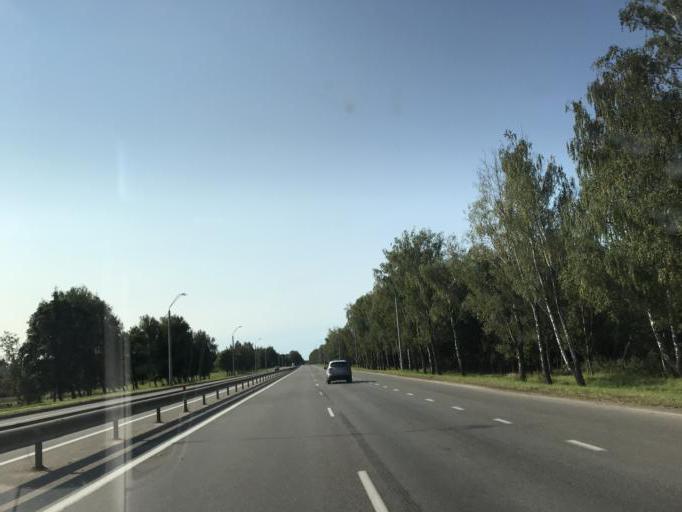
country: BY
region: Mogilev
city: Buynichy
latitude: 53.8557
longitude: 30.2554
